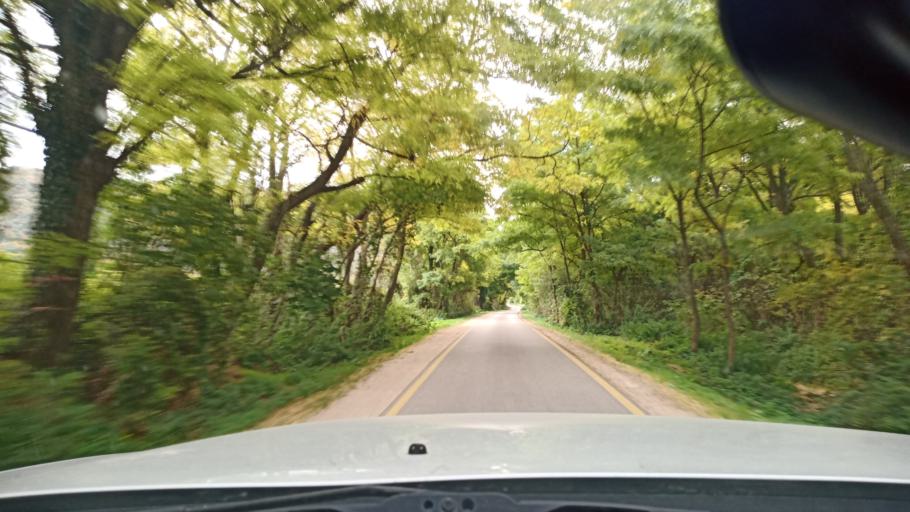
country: HU
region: Fejer
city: Mor
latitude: 47.3739
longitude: 18.2330
